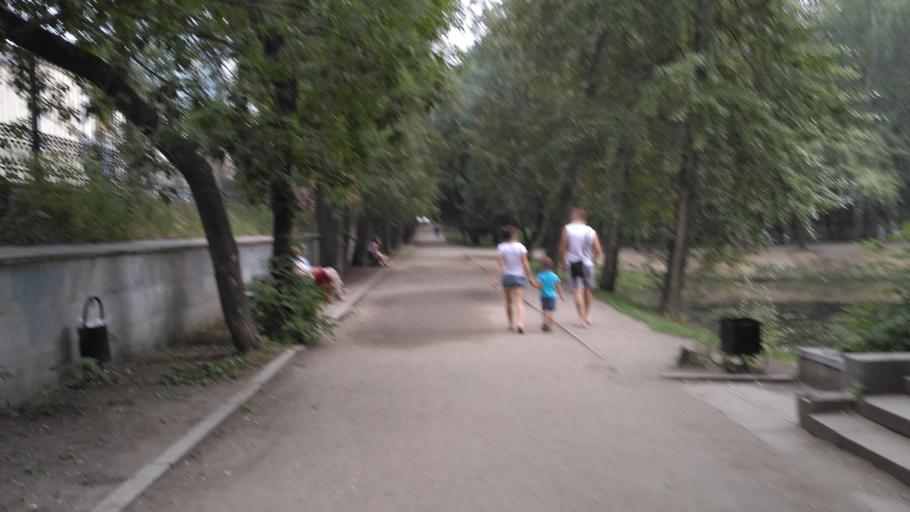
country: RU
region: Sverdlovsk
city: Yekaterinburg
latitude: 56.8469
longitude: 60.6150
